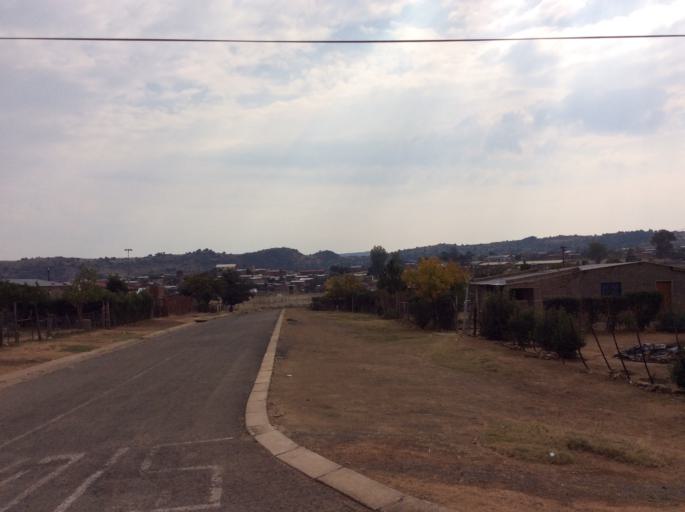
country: LS
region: Mafeteng
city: Mafeteng
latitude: -29.9866
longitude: 27.0081
